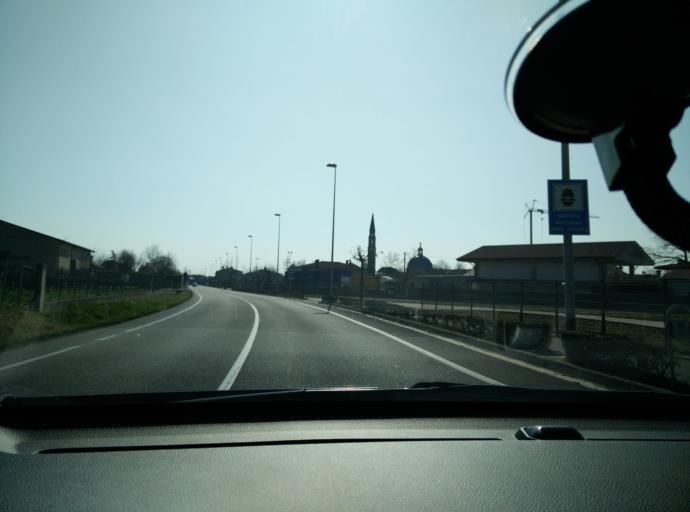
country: IT
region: Veneto
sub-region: Provincia di Treviso
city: San Michele di Piave
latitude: 45.8007
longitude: 12.3427
